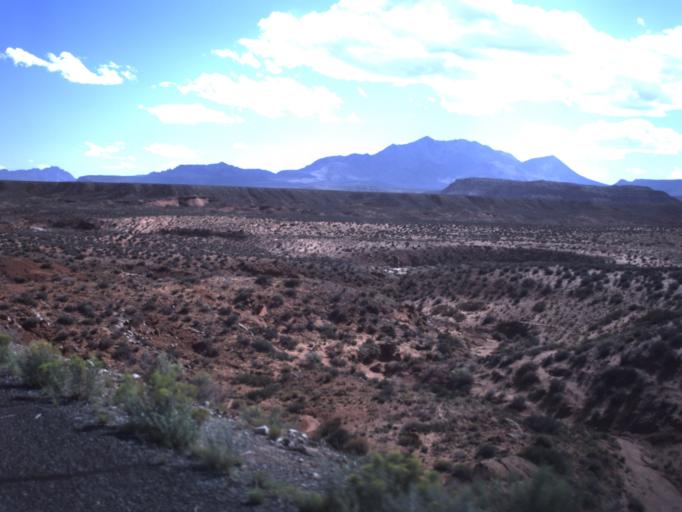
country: US
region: Utah
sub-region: Wayne County
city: Loa
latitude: 38.0714
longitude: -110.6072
